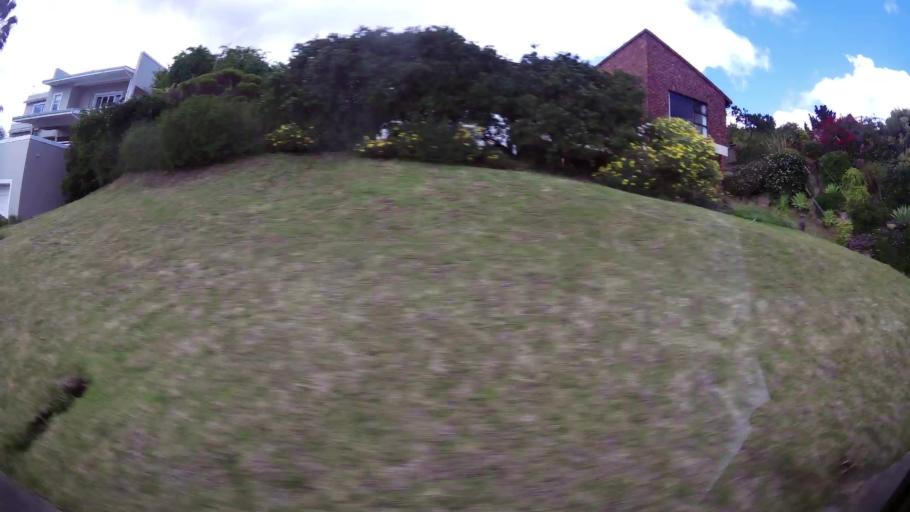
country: ZA
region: Western Cape
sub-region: Eden District Municipality
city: Knysna
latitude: -34.0648
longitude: 23.0816
